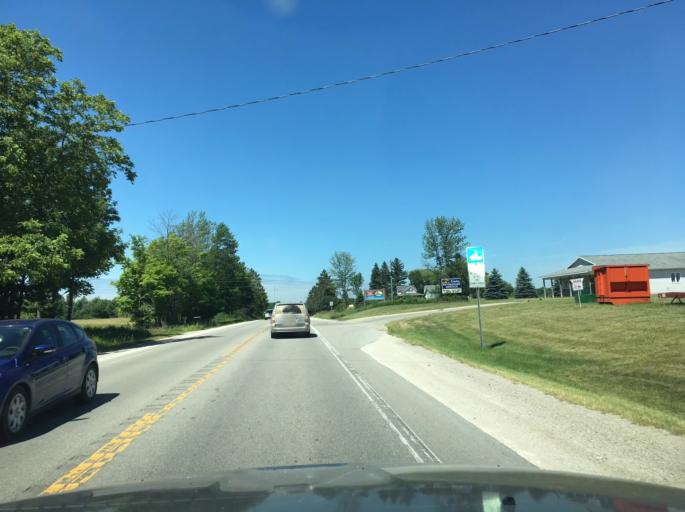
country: US
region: Michigan
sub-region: Osceola County
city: Reed City
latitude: 43.8877
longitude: -85.5658
